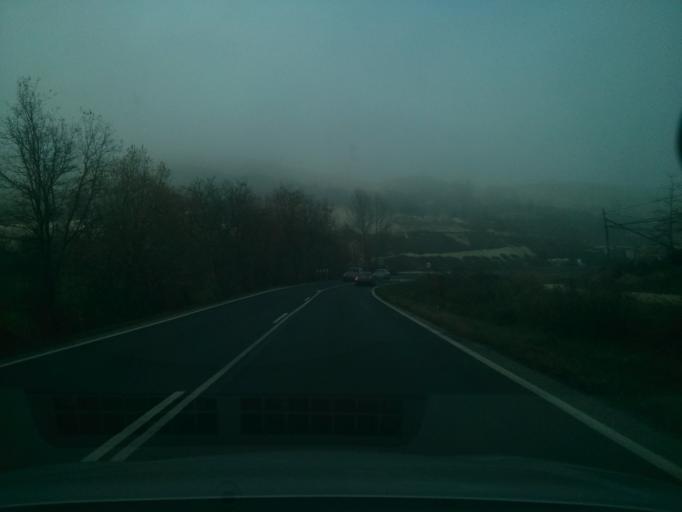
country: ES
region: Castille and Leon
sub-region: Provincia de Burgos
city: Medina de Pomar
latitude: 42.9091
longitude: -3.5903
